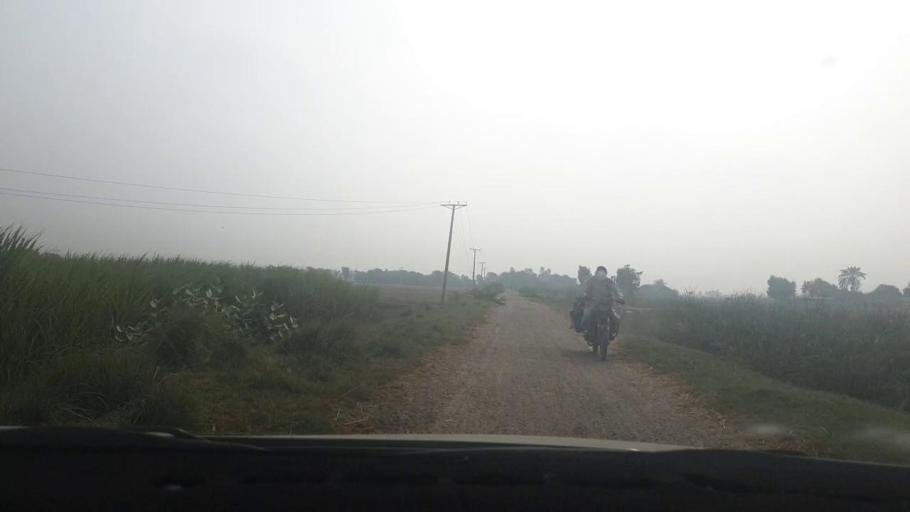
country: PK
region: Sindh
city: Tando Muhammad Khan
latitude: 25.1047
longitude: 68.5346
